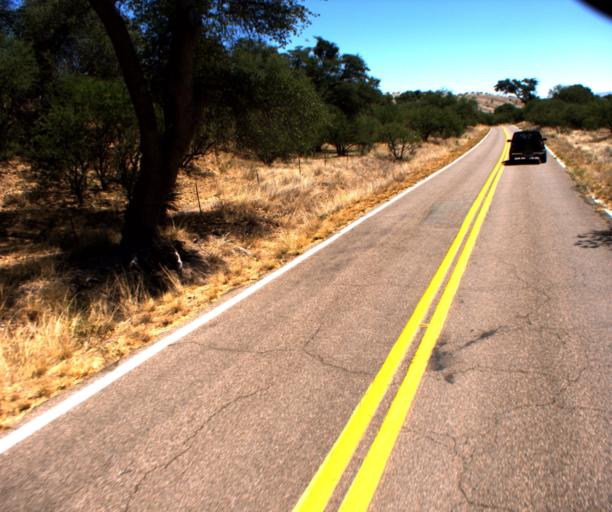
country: US
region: Arizona
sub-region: Santa Cruz County
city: Rio Rico
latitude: 31.3904
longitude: -111.0475
